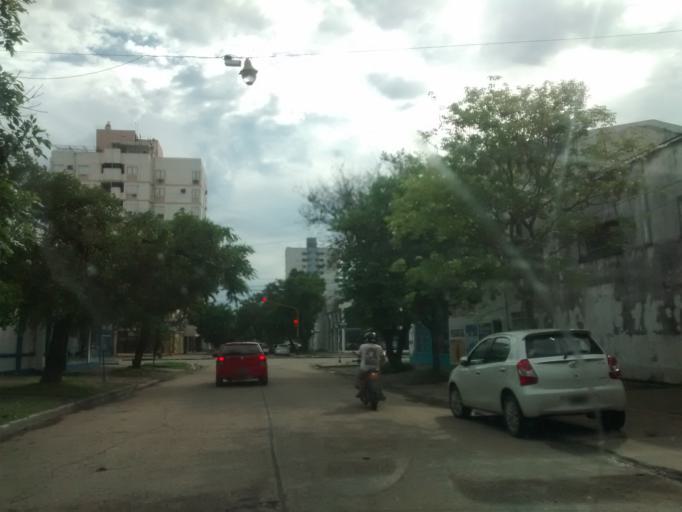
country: AR
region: Chaco
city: Resistencia
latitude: -27.4420
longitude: -58.9959
